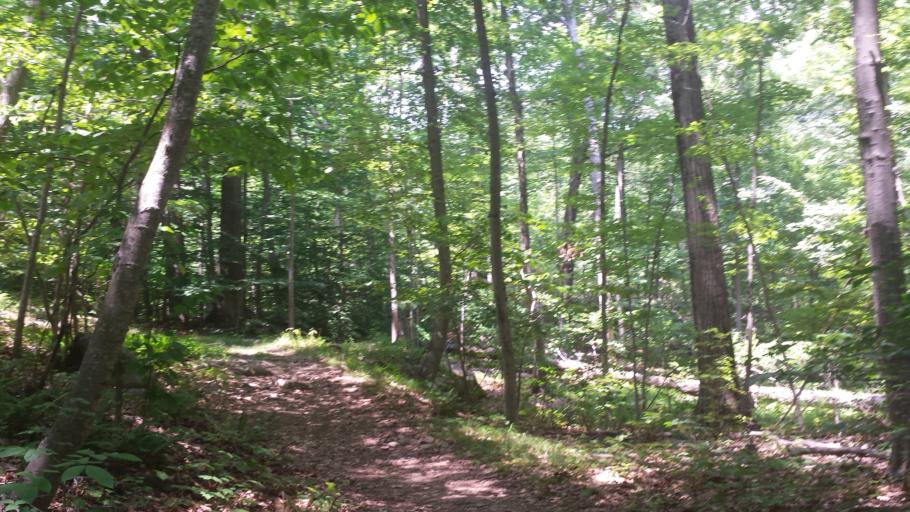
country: US
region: New York
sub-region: Westchester County
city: Valhalla
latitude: 41.0797
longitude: -73.7543
